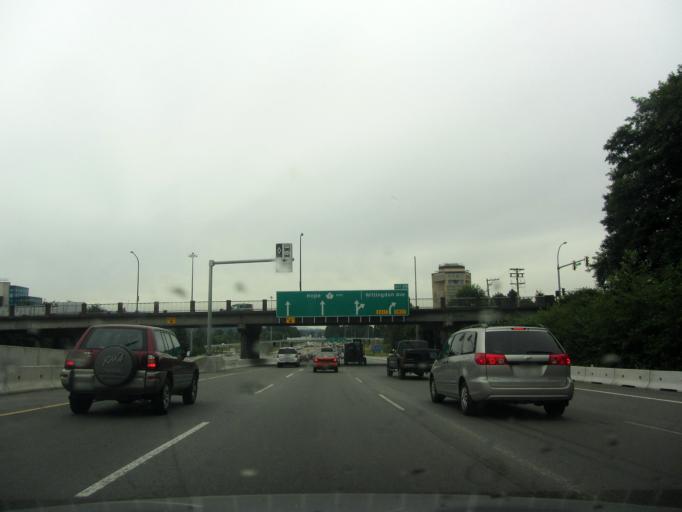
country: CA
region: British Columbia
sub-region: Fraser Valley Regional District
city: North Vancouver
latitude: 49.2693
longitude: -123.0328
